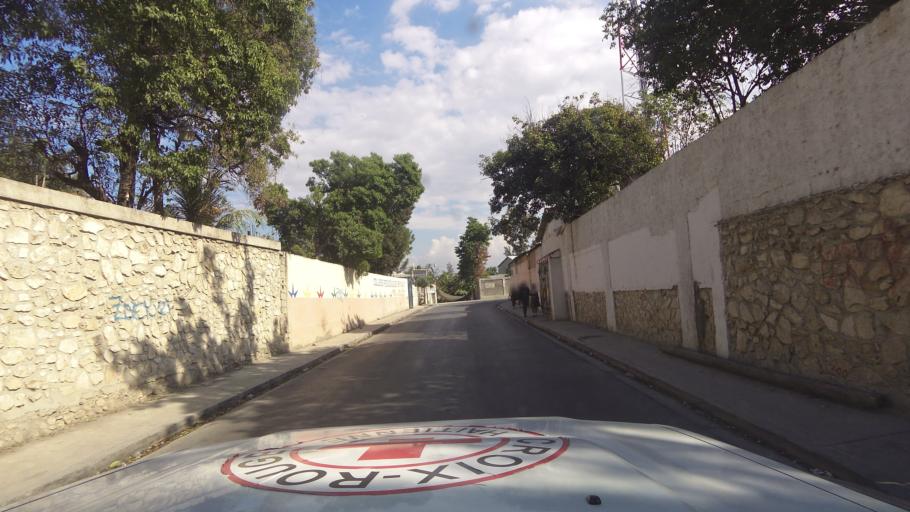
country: HT
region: Ouest
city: Petionville
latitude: 18.5299
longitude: -72.2821
